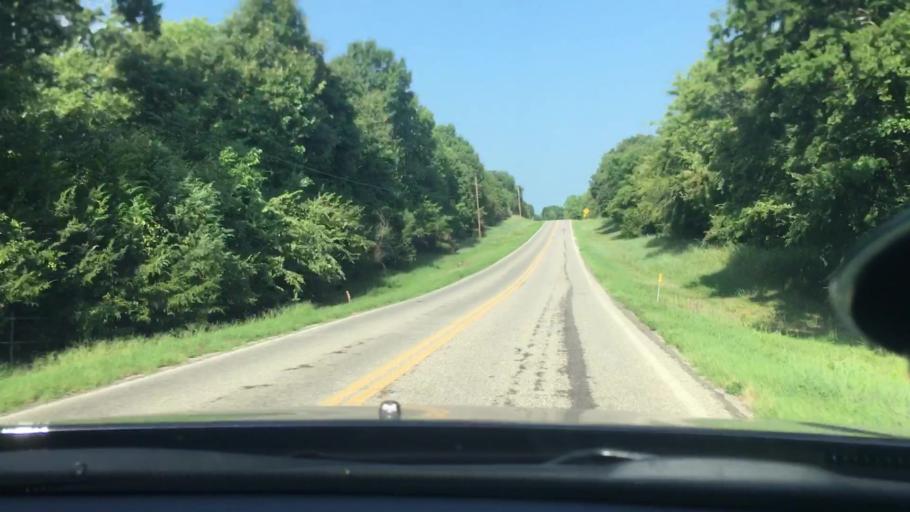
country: US
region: Oklahoma
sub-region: Johnston County
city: Tishomingo
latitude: 34.2088
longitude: -96.6295
